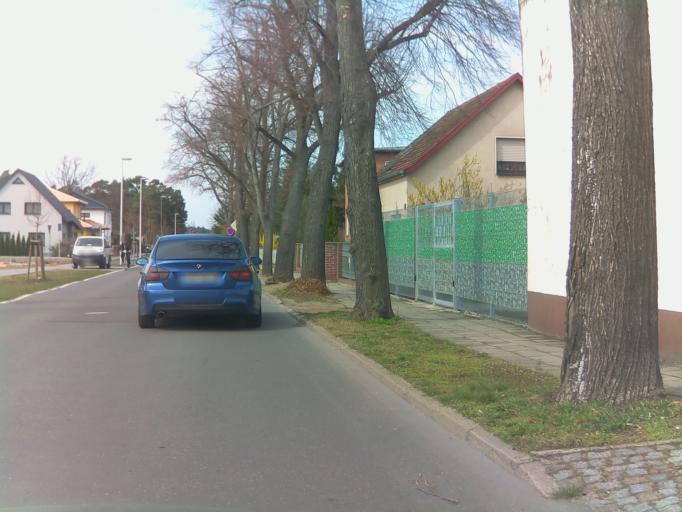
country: DE
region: Brandenburg
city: Cottbus
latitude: 51.7776
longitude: 14.3307
